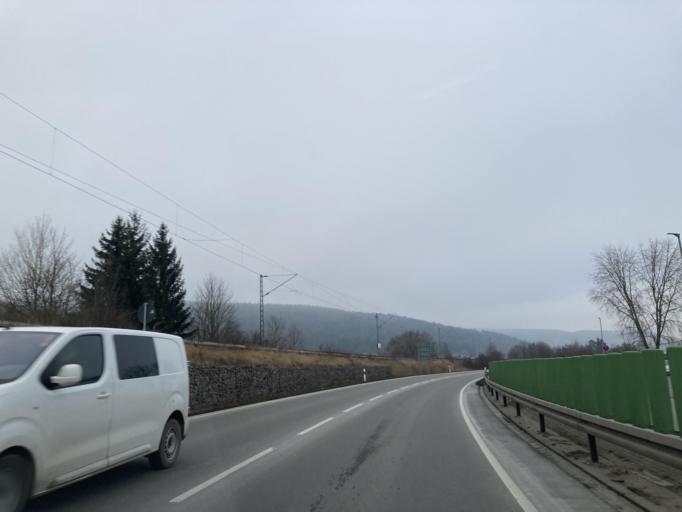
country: DE
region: Baden-Wuerttemberg
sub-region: Freiburg Region
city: Wurmlingen
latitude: 47.9663
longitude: 8.7845
